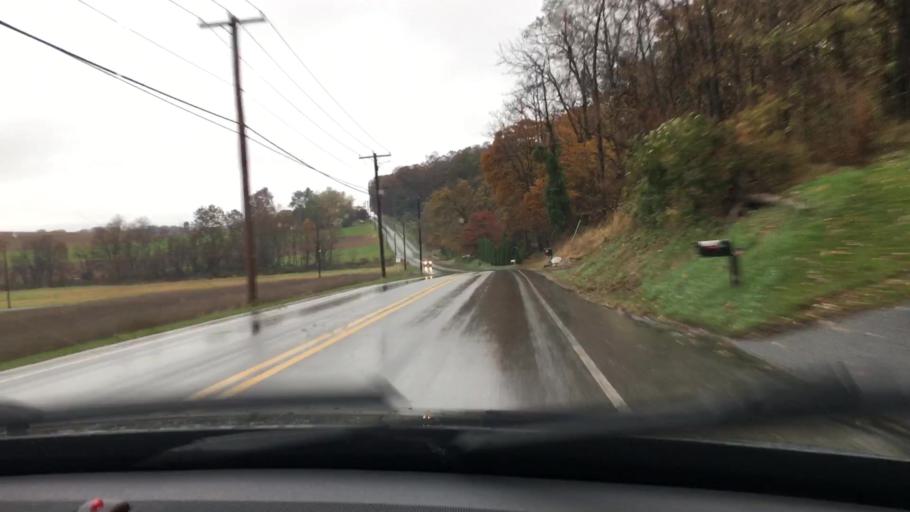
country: US
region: Pennsylvania
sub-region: Lancaster County
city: Quarryville
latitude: 39.8628
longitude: -76.2629
